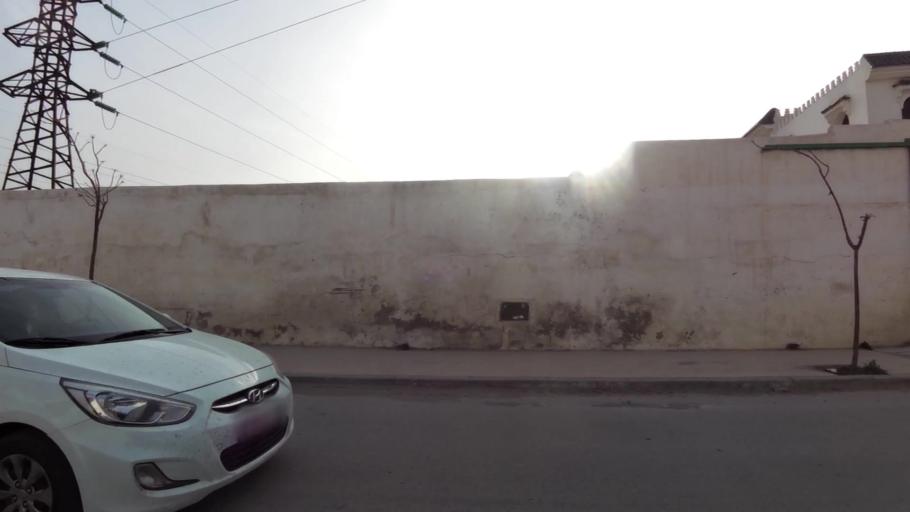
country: MA
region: Tanger-Tetouan
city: Tetouan
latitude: 35.5633
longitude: -5.3928
